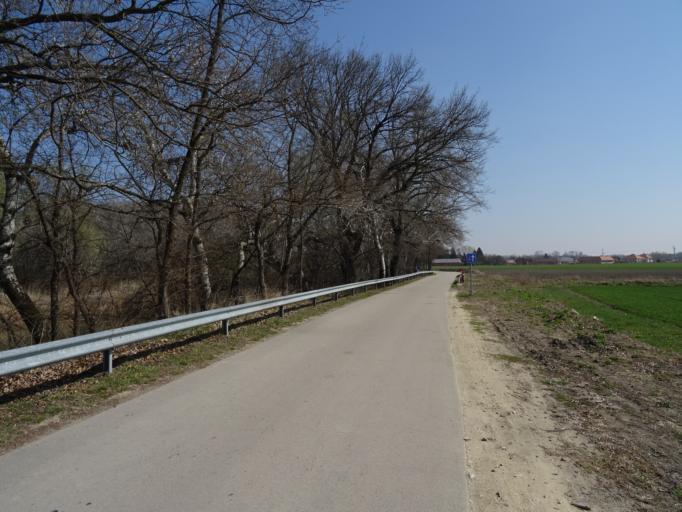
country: HU
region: Pest
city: Rackeve
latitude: 47.1247
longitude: 18.9573
